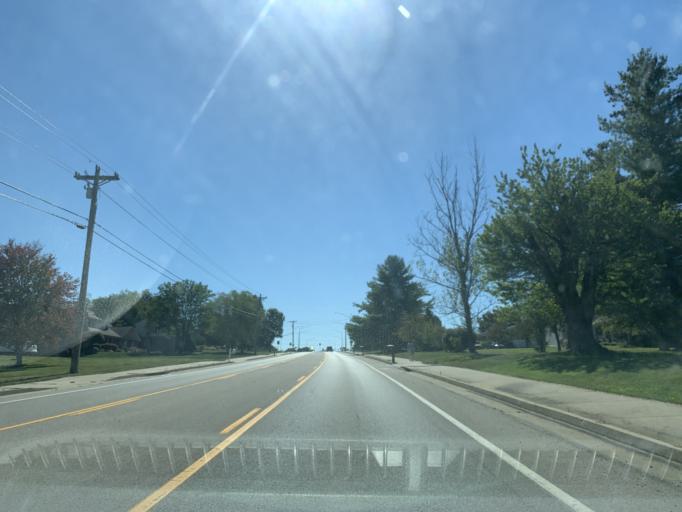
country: US
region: Kentucky
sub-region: Boone County
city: Francisville
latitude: 39.1010
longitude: -84.7209
